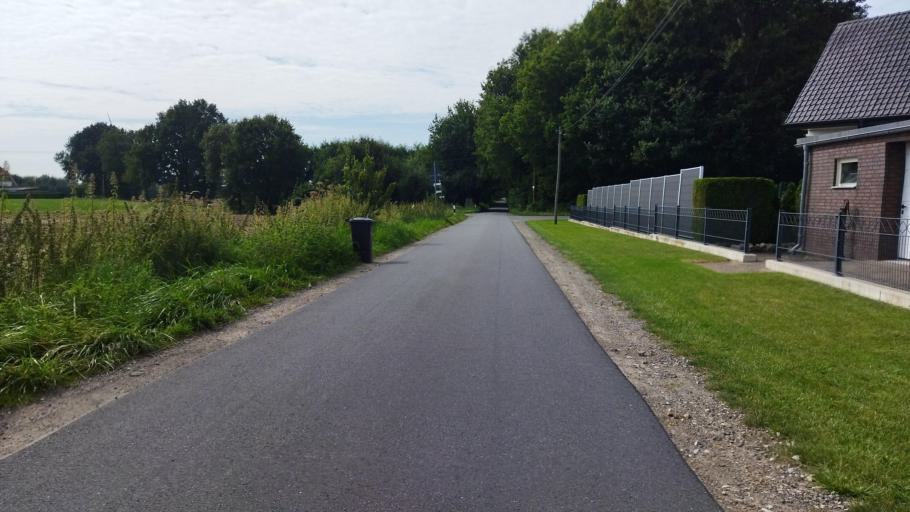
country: DE
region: Lower Saxony
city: Bad Iburg
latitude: 52.1380
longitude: 8.0151
